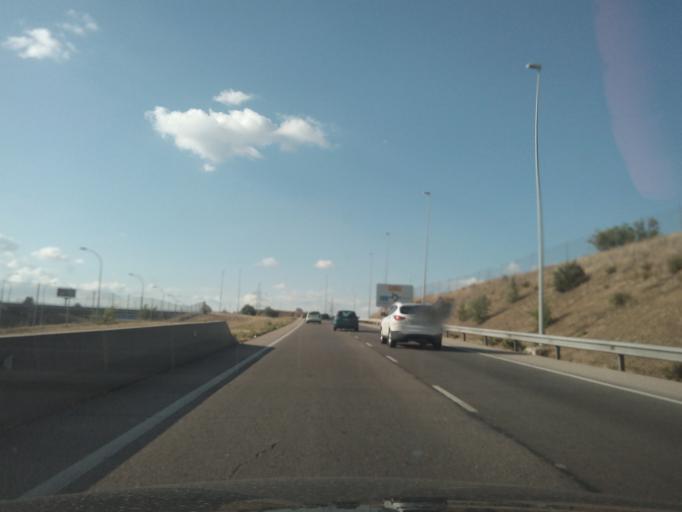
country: ES
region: Madrid
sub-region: Provincia de Madrid
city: San Sebastian de los Reyes
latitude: 40.5446
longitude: -3.6076
